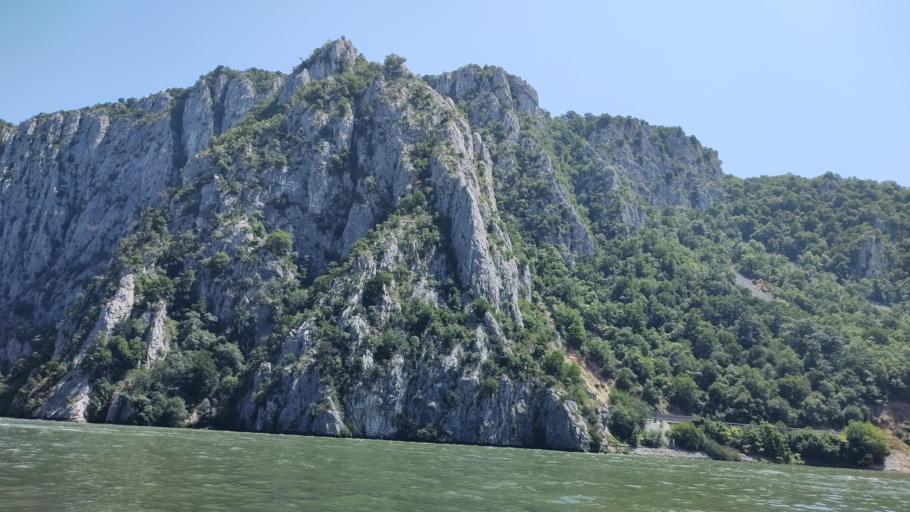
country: RO
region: Mehedinti
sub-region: Comuna Dubova
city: Dubova
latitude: 44.6106
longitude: 22.2711
